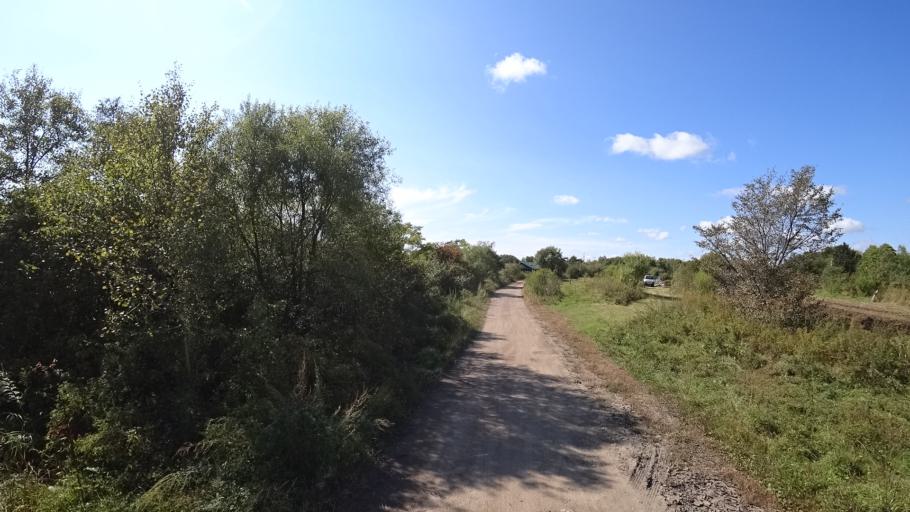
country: RU
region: Amur
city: Arkhara
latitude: 49.3992
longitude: 130.1284
